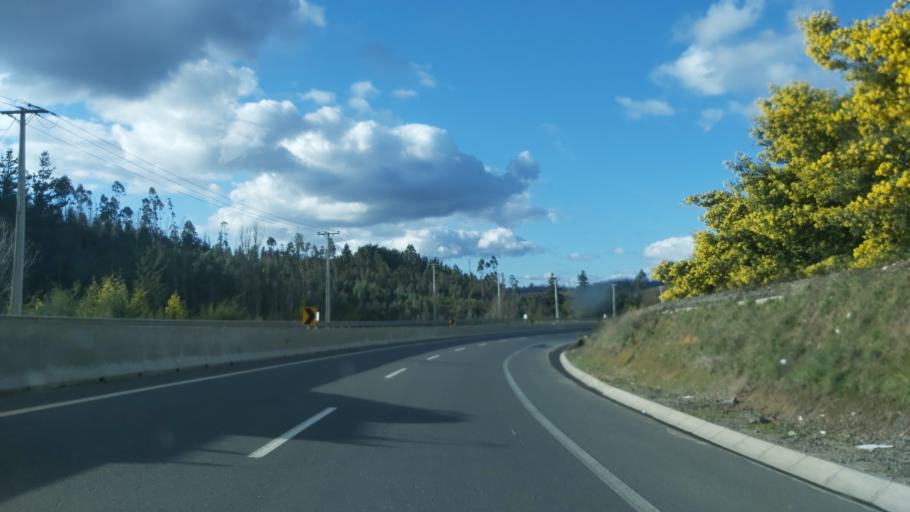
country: CL
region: Biobio
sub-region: Provincia de Concepcion
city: Penco
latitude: -36.8506
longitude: -72.9067
